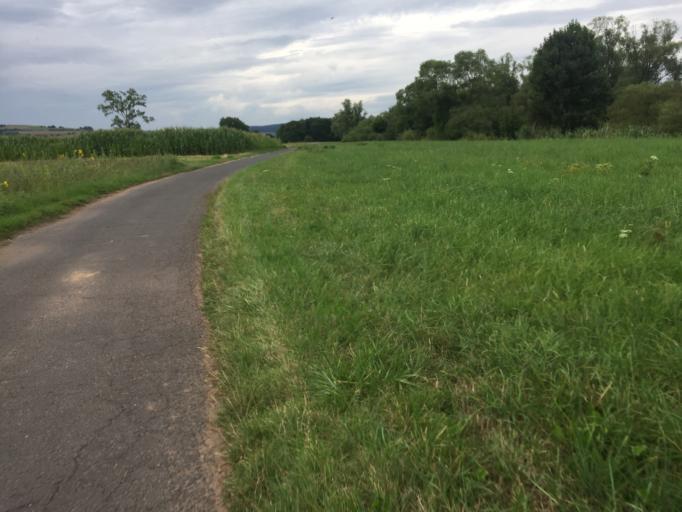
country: DE
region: Hesse
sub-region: Regierungsbezirk Kassel
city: Alheim
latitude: 51.0087
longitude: 9.6901
